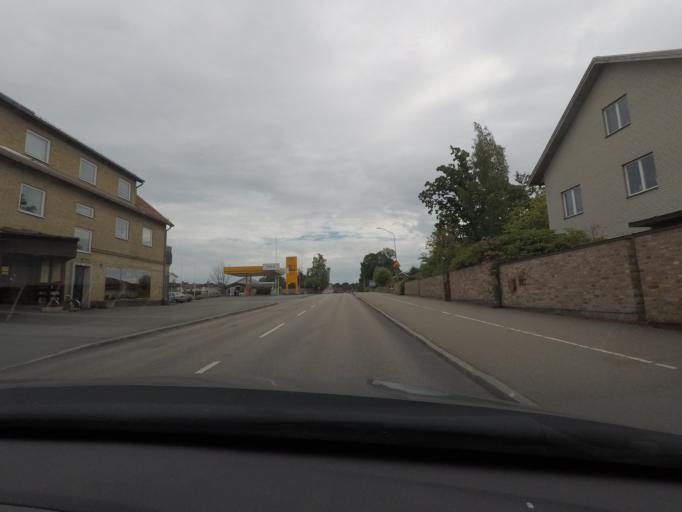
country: SE
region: Skane
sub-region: Osby Kommun
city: Osby
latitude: 56.3781
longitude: 14.0034
